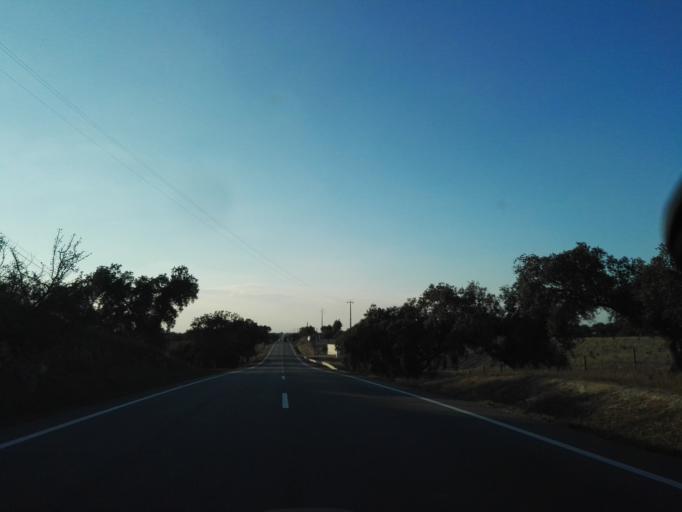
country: PT
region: Evora
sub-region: Arraiolos
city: Arraiolos
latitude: 38.8344
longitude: -7.8497
